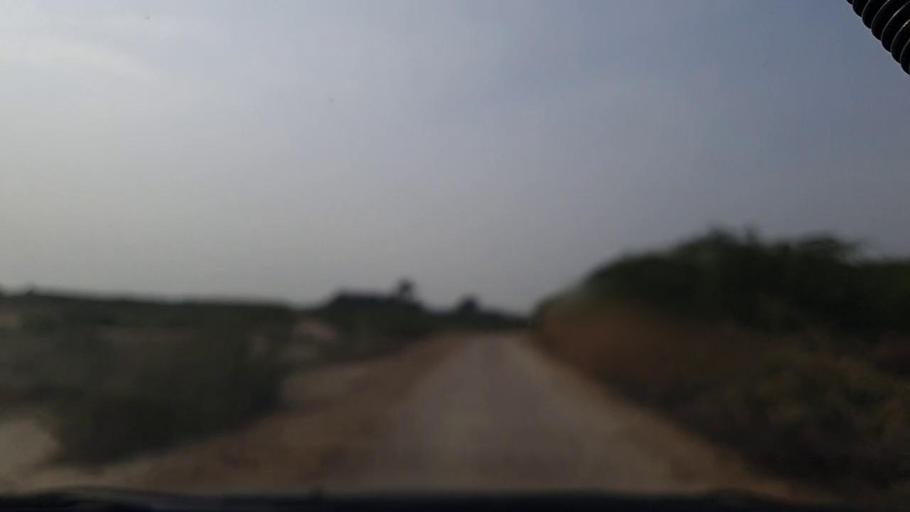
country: PK
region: Sindh
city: Thatta
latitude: 24.6131
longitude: 67.9546
